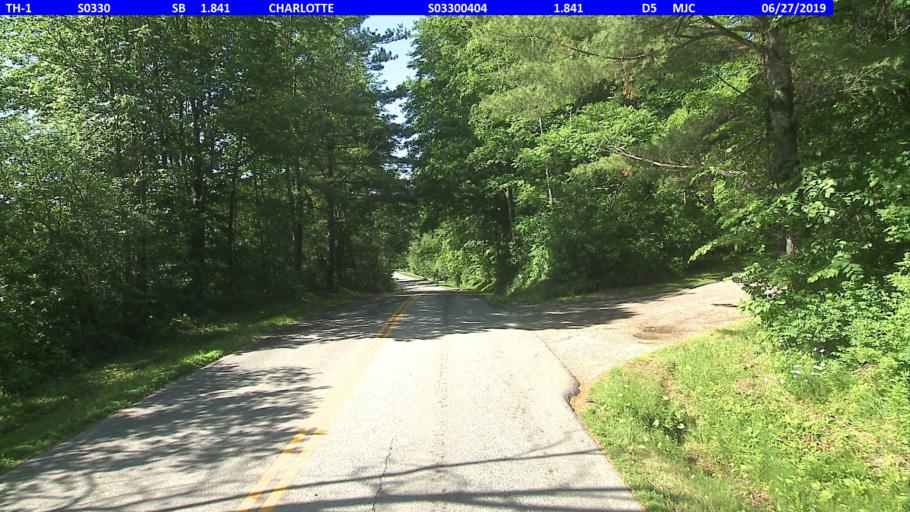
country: US
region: Vermont
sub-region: Chittenden County
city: Hinesburg
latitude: 44.3455
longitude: -73.1941
